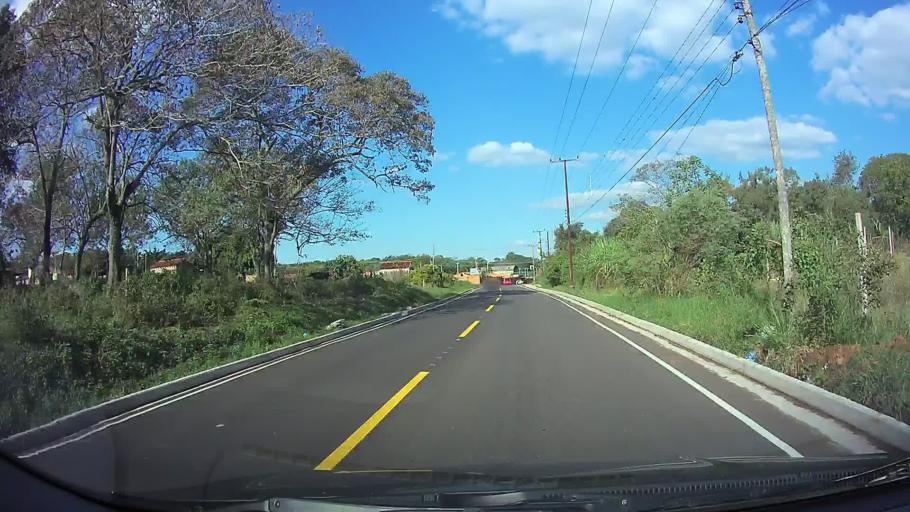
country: PY
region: Central
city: San Lorenzo
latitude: -25.2672
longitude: -57.4699
